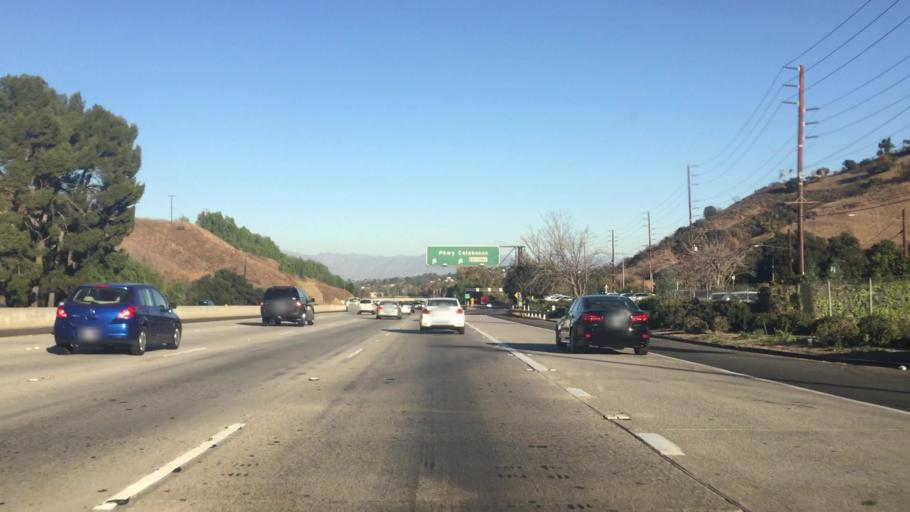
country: US
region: California
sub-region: Los Angeles County
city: Hidden Hills
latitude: 34.1505
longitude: -118.6611
